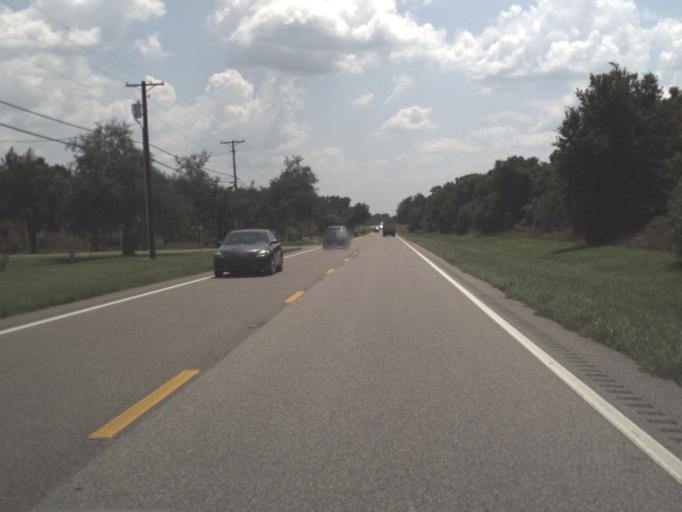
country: US
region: Florida
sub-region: Hillsborough County
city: Sun City Center
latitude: 27.6844
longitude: -82.3452
